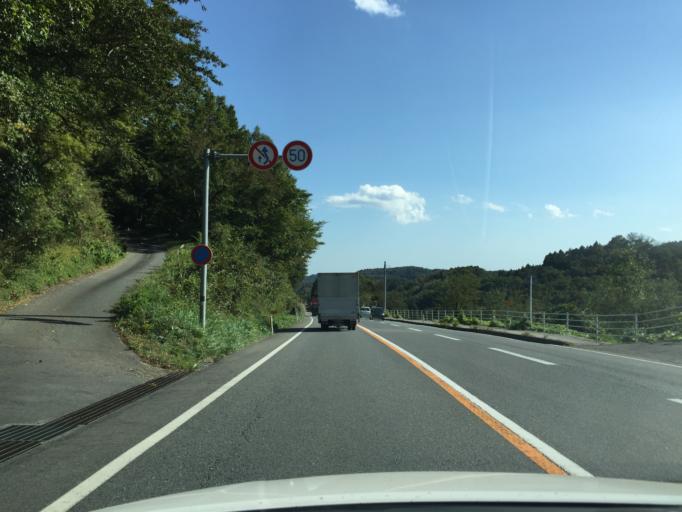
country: JP
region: Fukushima
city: Iwaki
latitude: 37.0787
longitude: 140.8169
